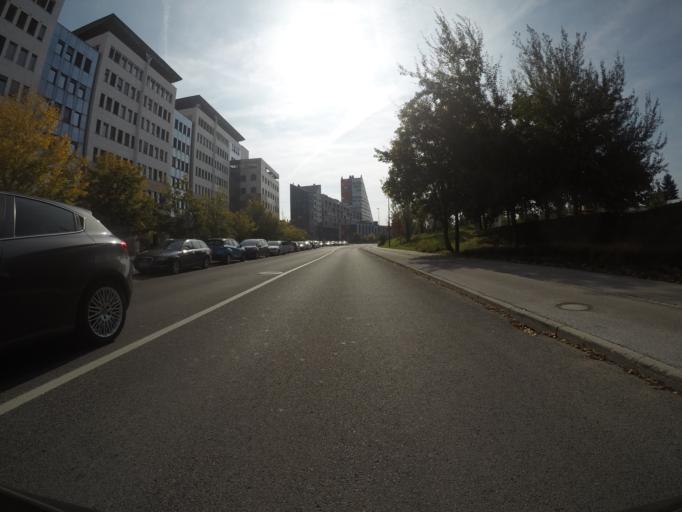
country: SI
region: Ljubljana
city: Ljubljana
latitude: 46.0629
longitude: 14.5132
